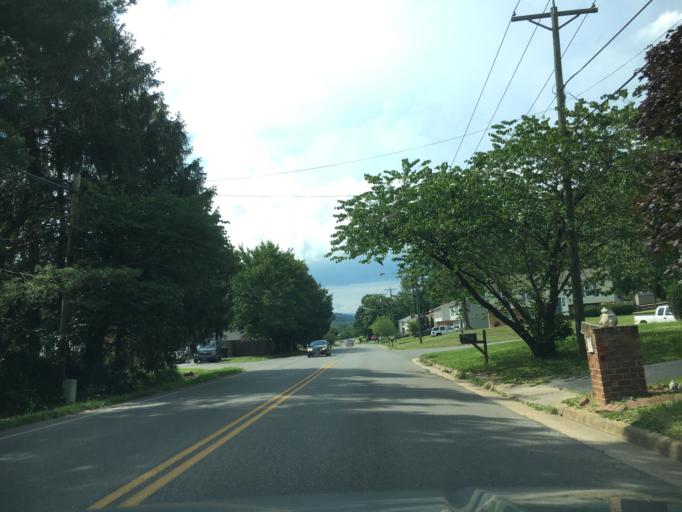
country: US
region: Virginia
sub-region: Roanoke County
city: Cave Spring
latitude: 37.2093
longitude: -80.0108
